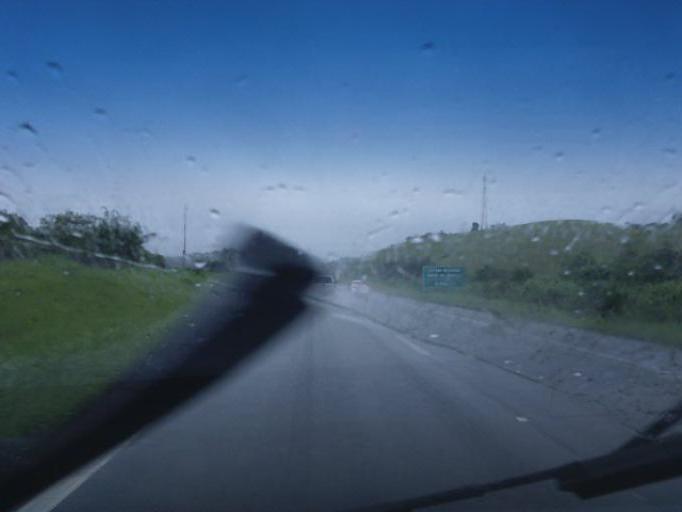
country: BR
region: Sao Paulo
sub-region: Registro
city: Registro
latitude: -24.4106
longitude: -47.7518
